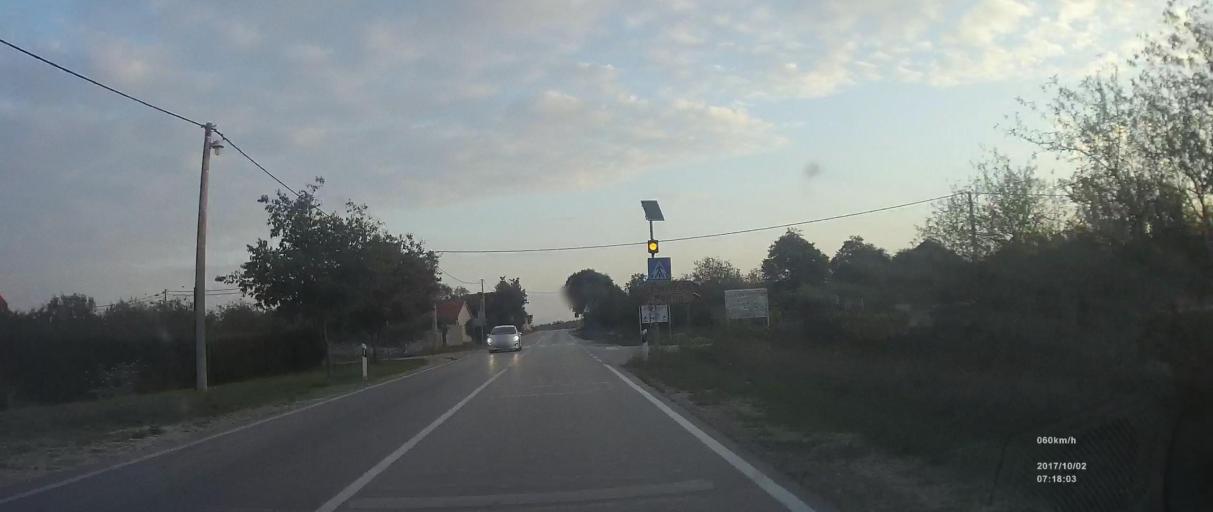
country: HR
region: Zadarska
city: Benkovac
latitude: 44.0150
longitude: 15.5942
